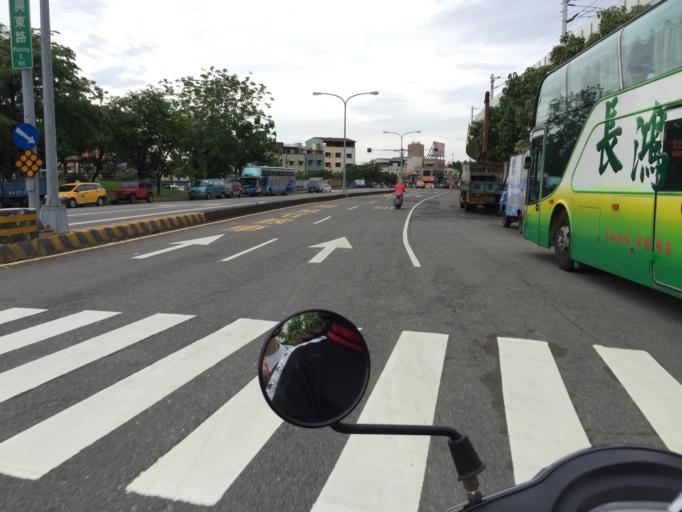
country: TW
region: Taiwan
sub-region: Taichung City
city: Taichung
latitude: 24.1421
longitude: 120.6964
